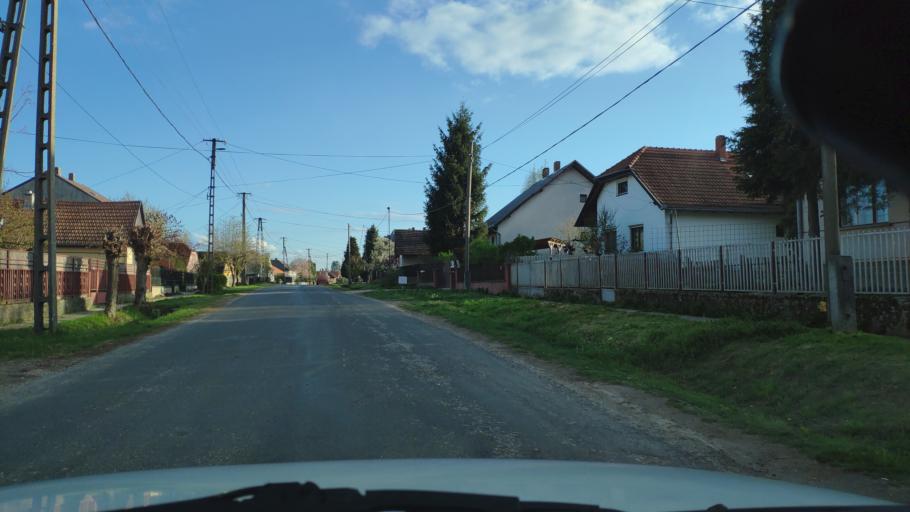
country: HU
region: Zala
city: Zalakomar
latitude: 46.4468
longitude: 17.1209
